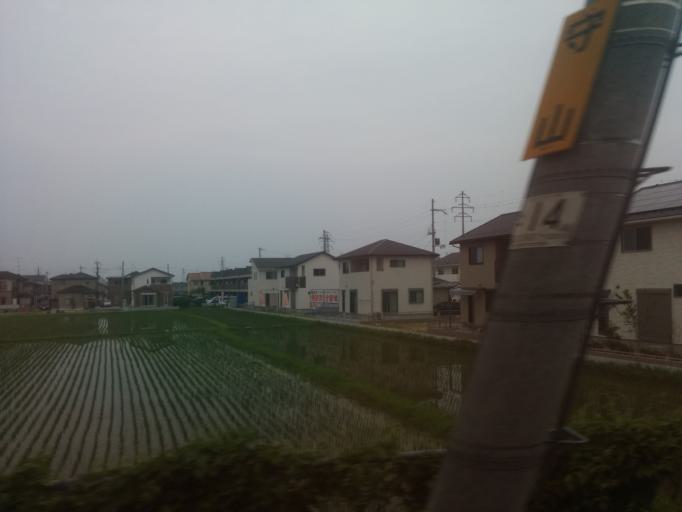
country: JP
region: Shiga Prefecture
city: Moriyama
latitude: 35.0431
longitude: 135.9868
